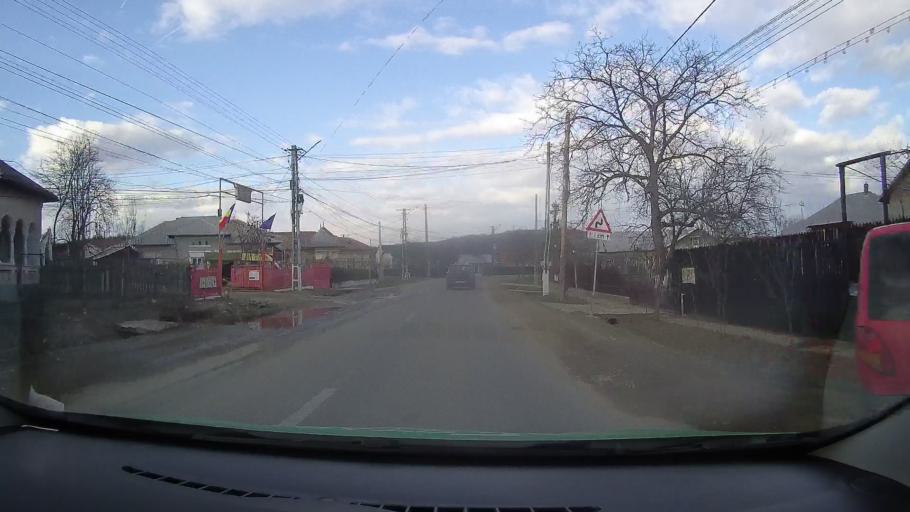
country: RO
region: Dambovita
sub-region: Comuna Gura Ocnitei
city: Gura Ocnitei
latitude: 44.9358
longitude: 25.5620
